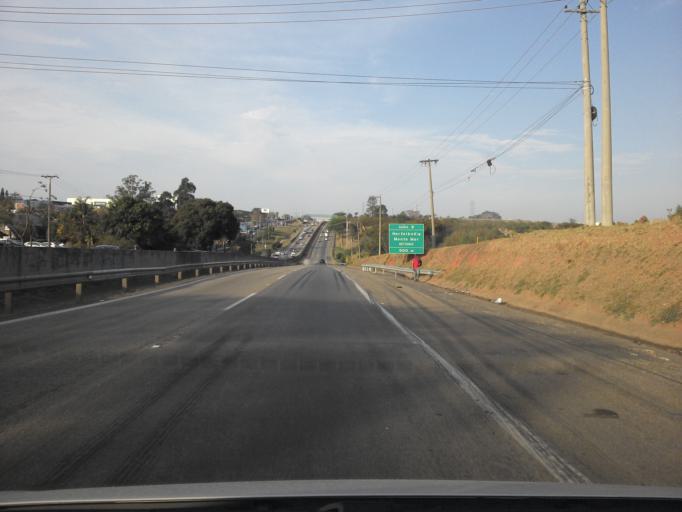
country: BR
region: Sao Paulo
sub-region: Hortolandia
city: Hortolandia
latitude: -22.8992
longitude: -47.1954
